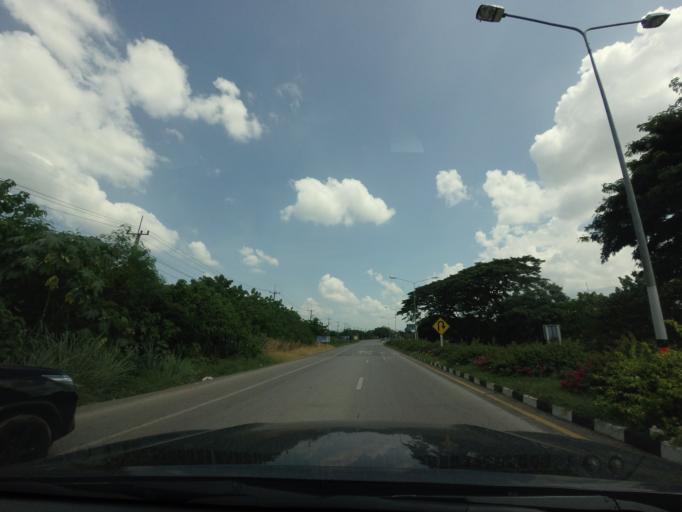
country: TH
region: Phetchabun
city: Phetchabun
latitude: 16.2607
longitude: 101.0506
